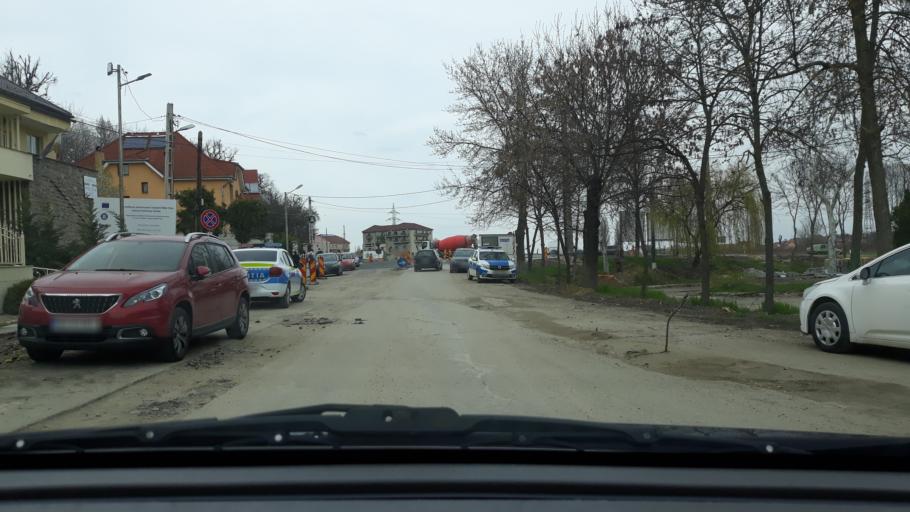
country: RO
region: Bihor
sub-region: Comuna Sanmartin
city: Sanmartin
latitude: 46.9958
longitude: 21.9787
